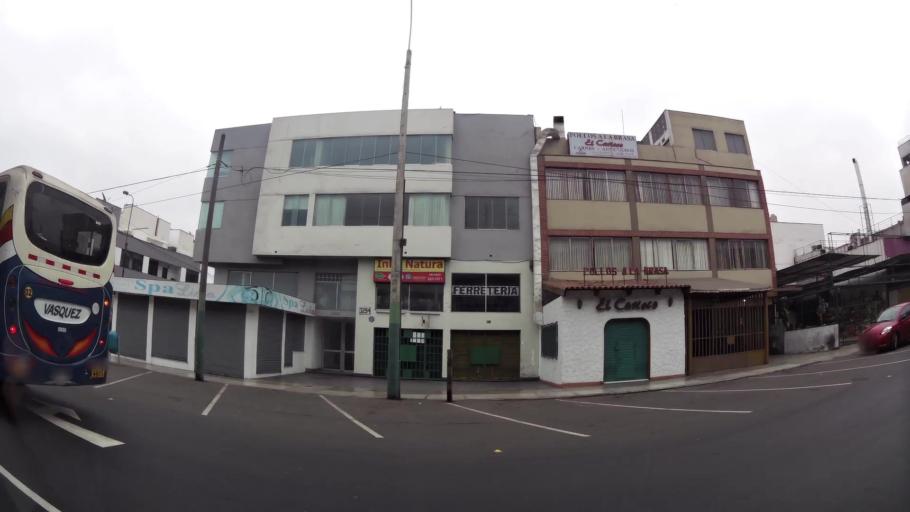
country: PE
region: Lima
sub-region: Lima
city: San Luis
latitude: -12.1030
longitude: -77.0015
